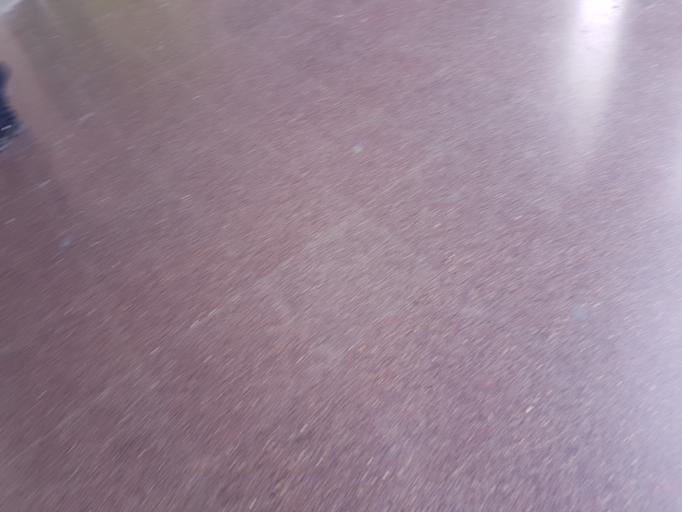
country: IT
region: Apulia
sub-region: Provincia di Bari
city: Bari
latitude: 41.1165
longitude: 16.8671
